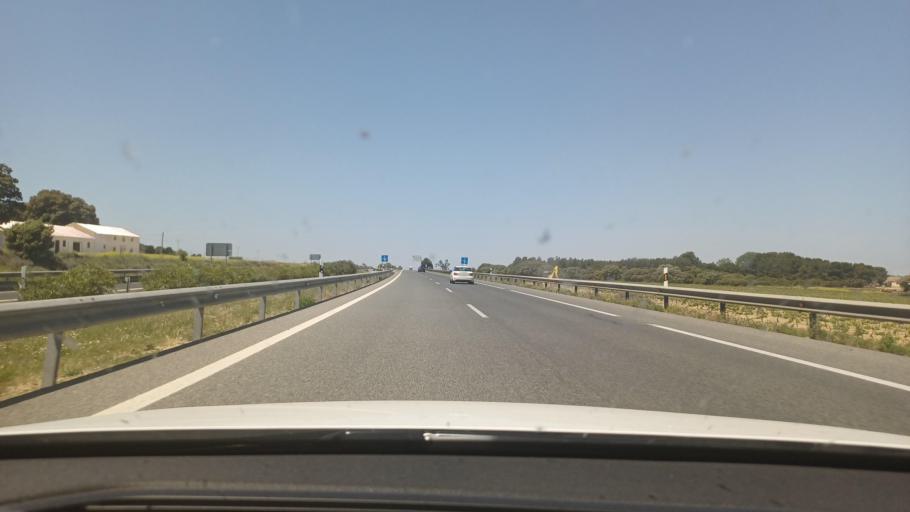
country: ES
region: Castille-La Mancha
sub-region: Provincia de Albacete
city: Corral-Rubio
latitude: 38.9006
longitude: -1.4762
